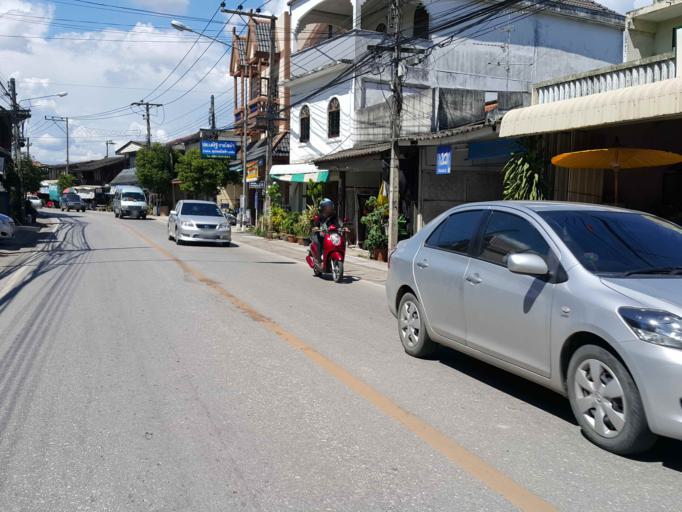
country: TH
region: Chiang Mai
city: San Kamphaeng
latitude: 18.7667
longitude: 99.0834
